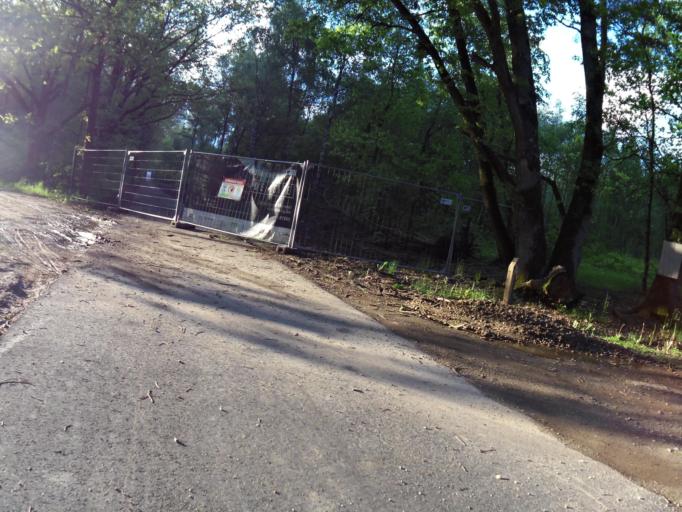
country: BE
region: Flanders
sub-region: Provincie Limburg
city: Zutendaal
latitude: 50.9517
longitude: 5.6190
